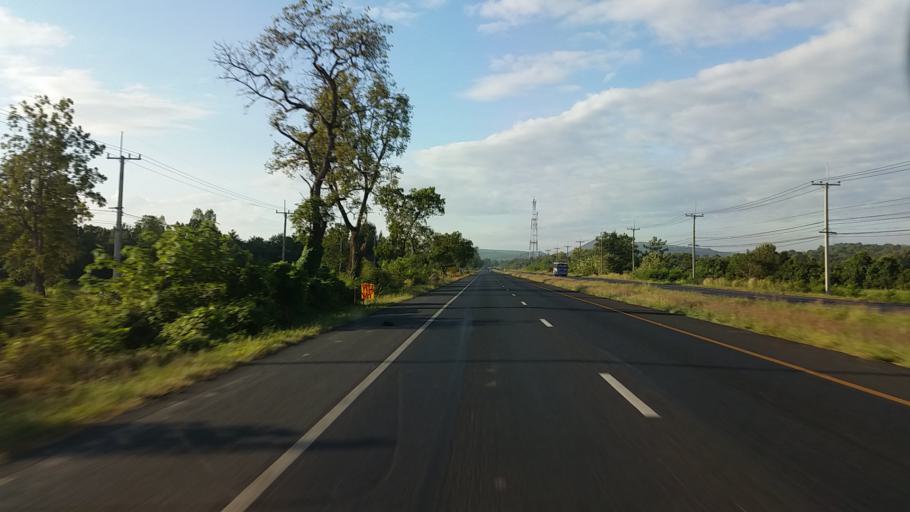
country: TH
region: Lop Buri
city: Phatthana Nikhom
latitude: 15.0043
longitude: 100.9398
